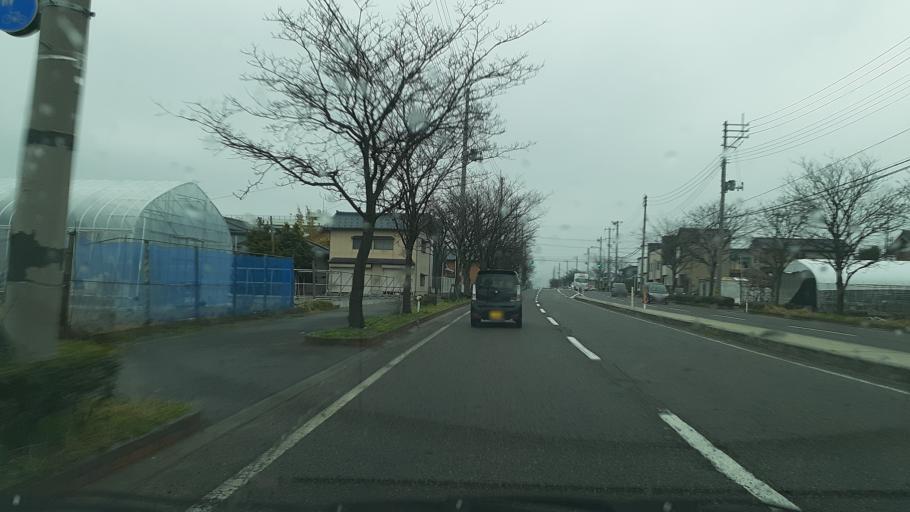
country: JP
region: Niigata
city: Kameda-honcho
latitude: 37.8803
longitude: 139.1280
